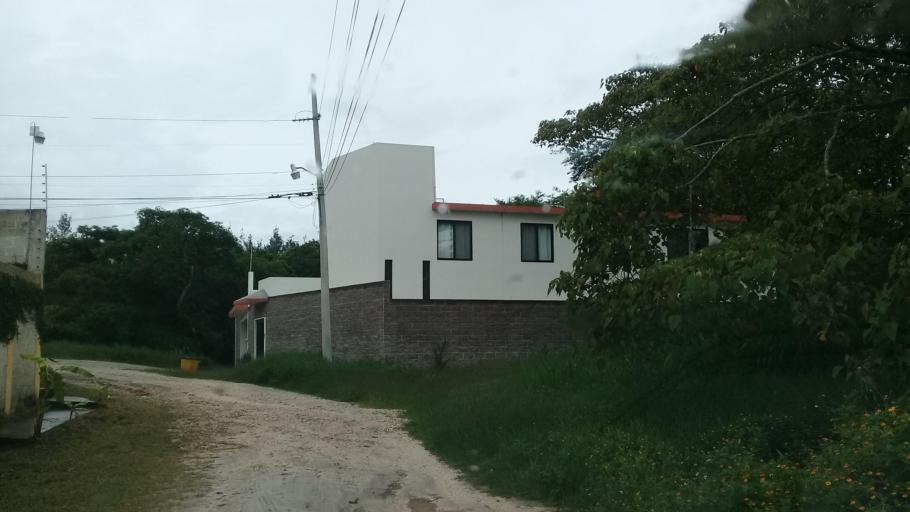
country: MX
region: Veracruz
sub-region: Emiliano Zapata
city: Jacarandas
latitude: 19.5029
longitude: -96.8405
